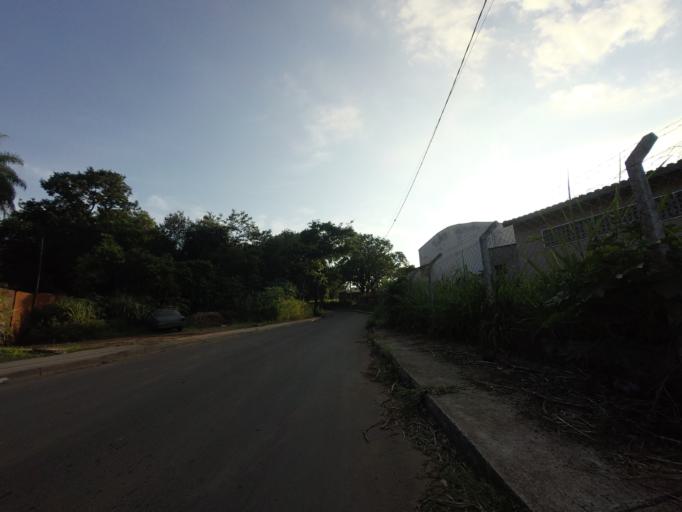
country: BR
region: Sao Paulo
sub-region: Piracicaba
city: Piracicaba
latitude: -22.7511
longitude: -47.6124
